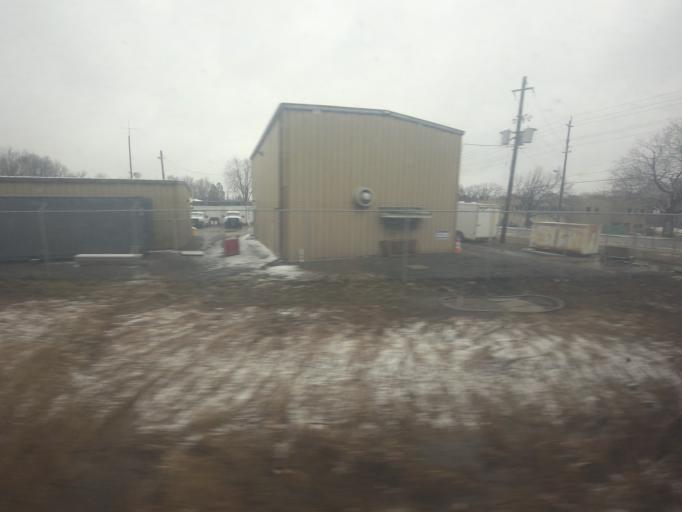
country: CA
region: Ontario
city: Brockville
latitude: 44.5979
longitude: -75.6897
